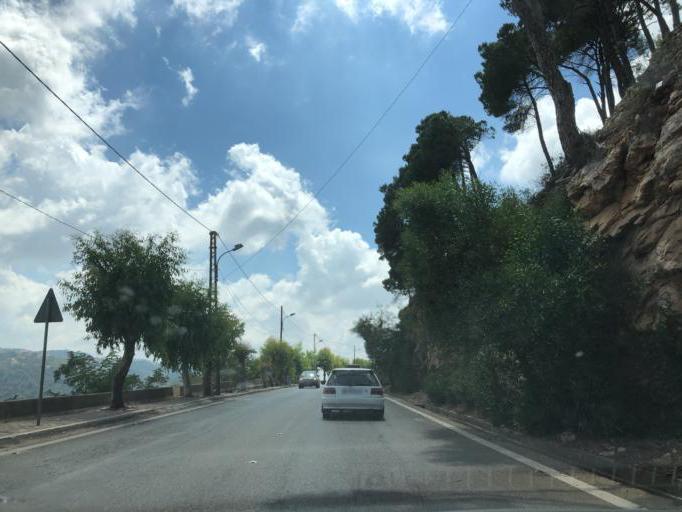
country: LB
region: Mont-Liban
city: Beit ed Dine
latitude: 33.6973
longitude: 35.5719
